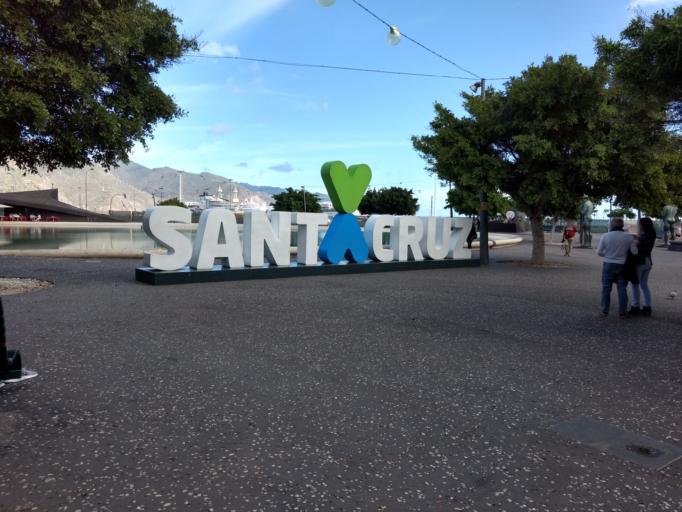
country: ES
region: Canary Islands
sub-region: Provincia de Santa Cruz de Tenerife
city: Santa Cruz de Tenerife
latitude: 28.4667
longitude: -16.2476
